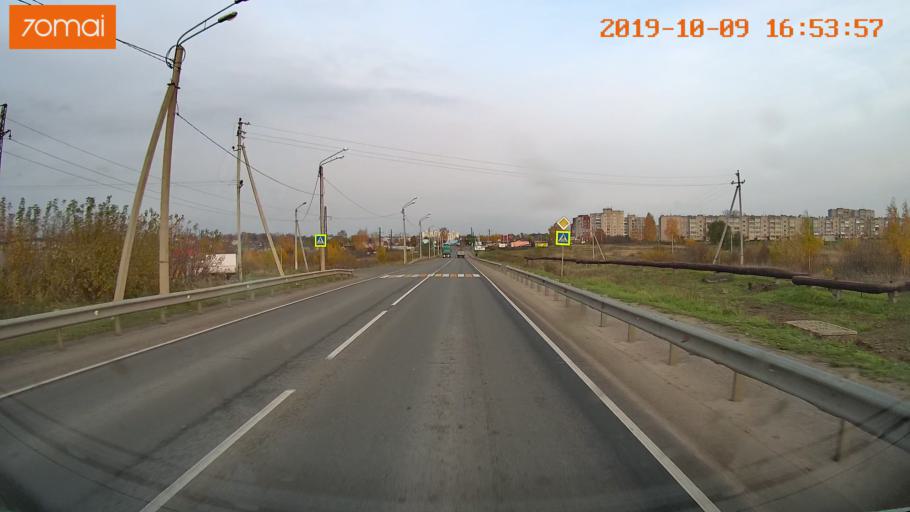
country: RU
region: Ivanovo
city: Privolzhsk
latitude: 57.3748
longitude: 41.2735
